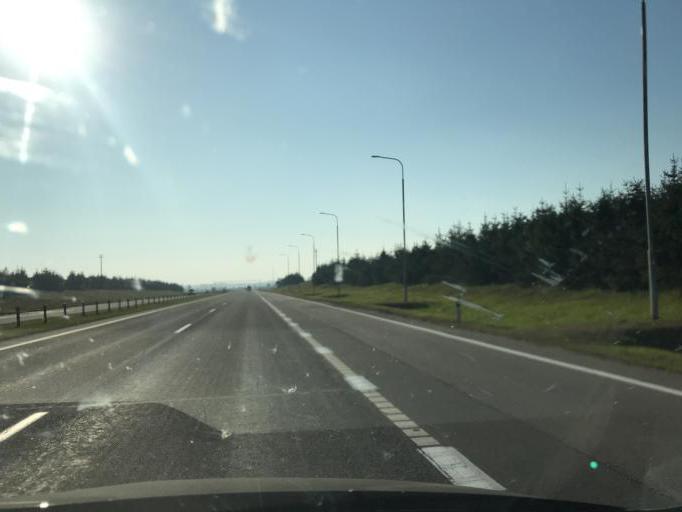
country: BY
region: Minsk
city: Haradzyeya
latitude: 53.3554
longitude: 26.4662
